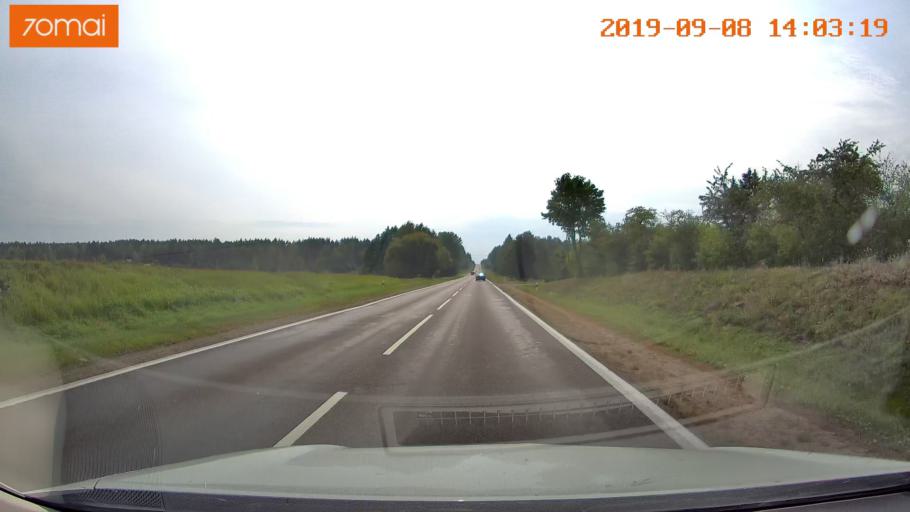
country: LT
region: Alytaus apskritis
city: Druskininkai
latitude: 54.1143
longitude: 24.2066
